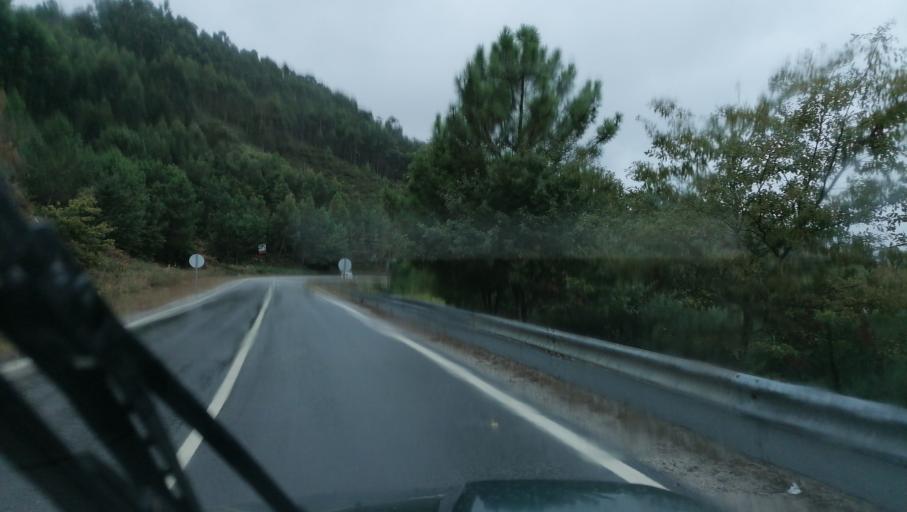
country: PT
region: Vila Real
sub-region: Ribeira de Pena
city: Ribeira de Pena
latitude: 41.5222
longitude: -7.8256
